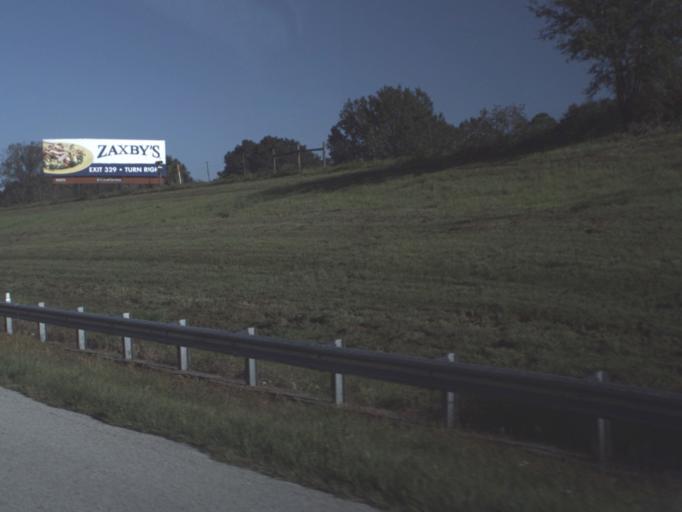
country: US
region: Florida
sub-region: Sumter County
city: Wildwood
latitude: 28.8199
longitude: -82.0203
